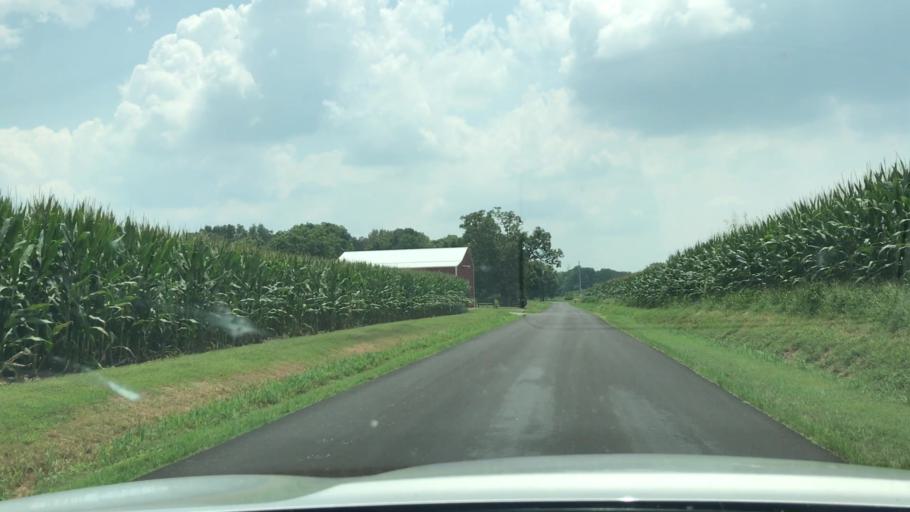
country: US
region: Kentucky
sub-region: Todd County
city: Elkton
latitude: 36.7769
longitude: -87.1449
